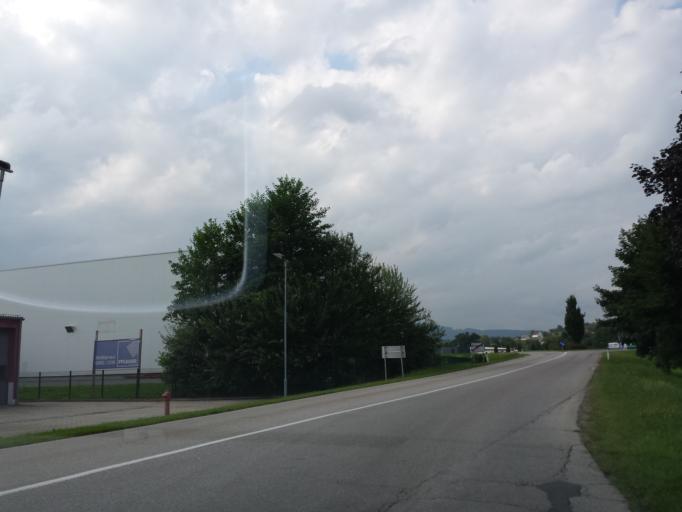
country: AT
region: Styria
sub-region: Politischer Bezirk Deutschlandsberg
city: Rassach
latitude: 46.8299
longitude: 15.2578
